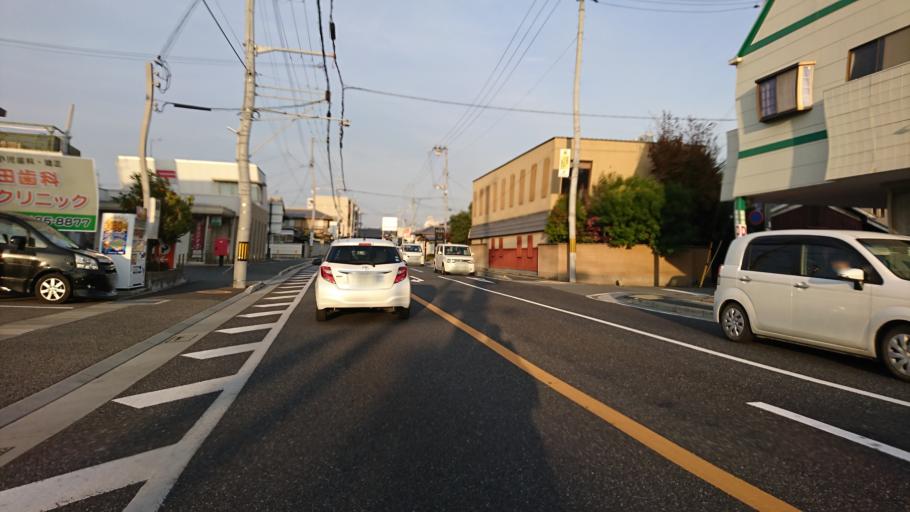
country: JP
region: Hyogo
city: Kakogawacho-honmachi
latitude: 34.7463
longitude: 134.8640
